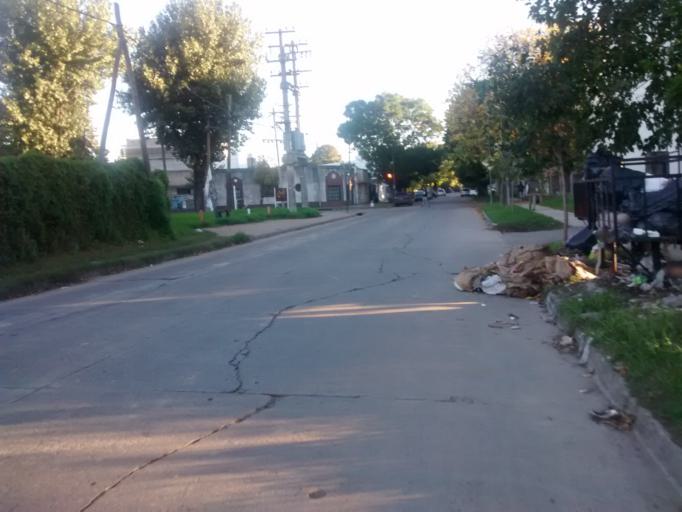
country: AR
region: Buenos Aires
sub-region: Partido de La Plata
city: La Plata
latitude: -34.9129
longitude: -57.9247
